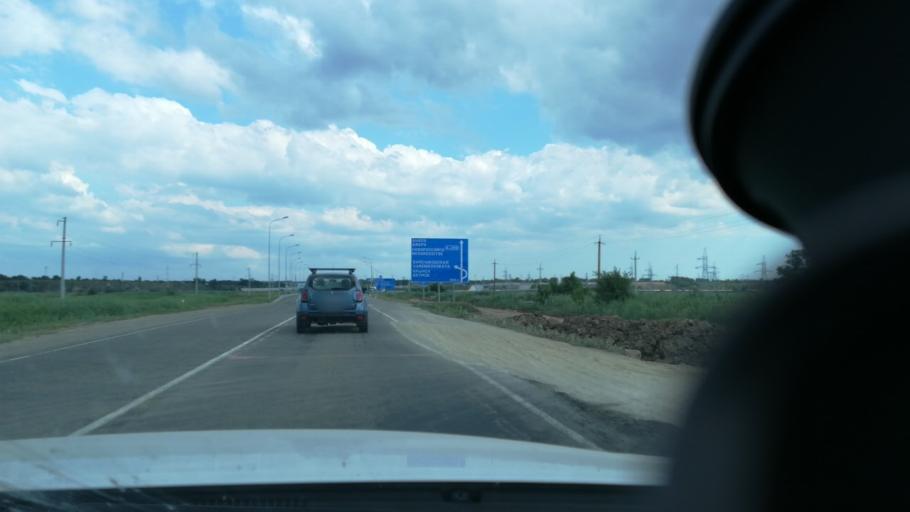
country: RU
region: Krasnodarskiy
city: Dzhiginka
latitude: 45.1438
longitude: 37.3134
